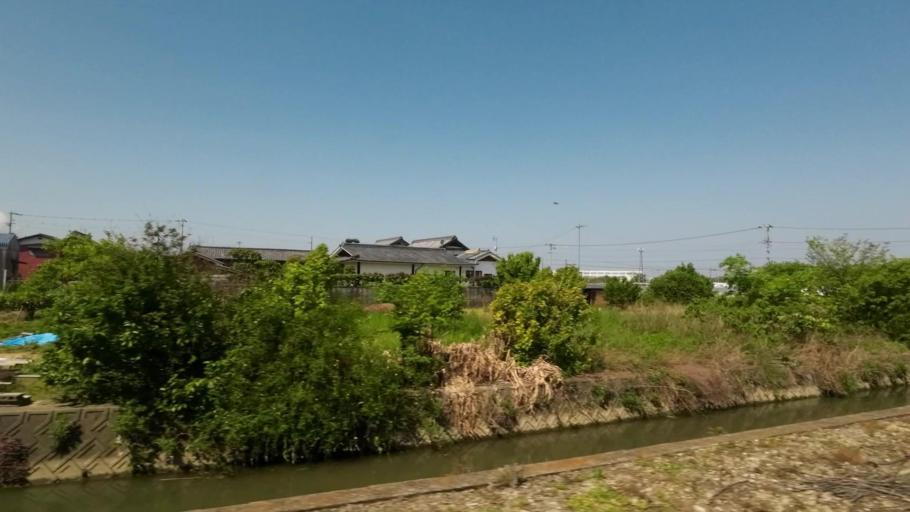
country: JP
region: Kagawa
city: Kan'onjicho
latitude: 34.1103
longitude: 133.6494
